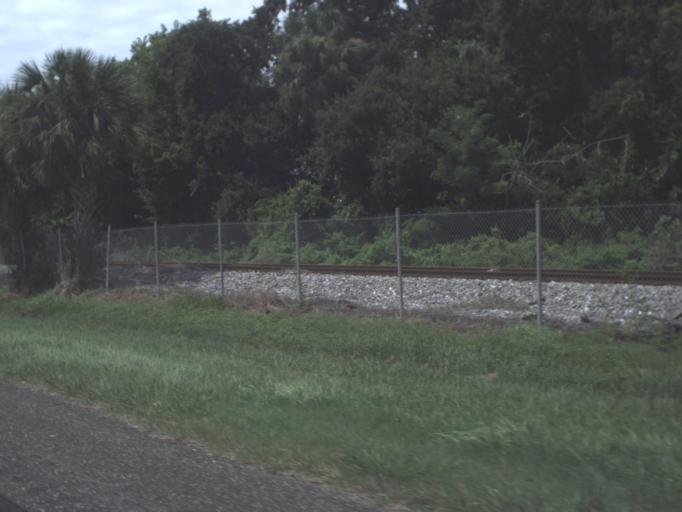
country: US
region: Florida
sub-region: Hillsborough County
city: Tampa
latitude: 27.9225
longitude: -82.4912
